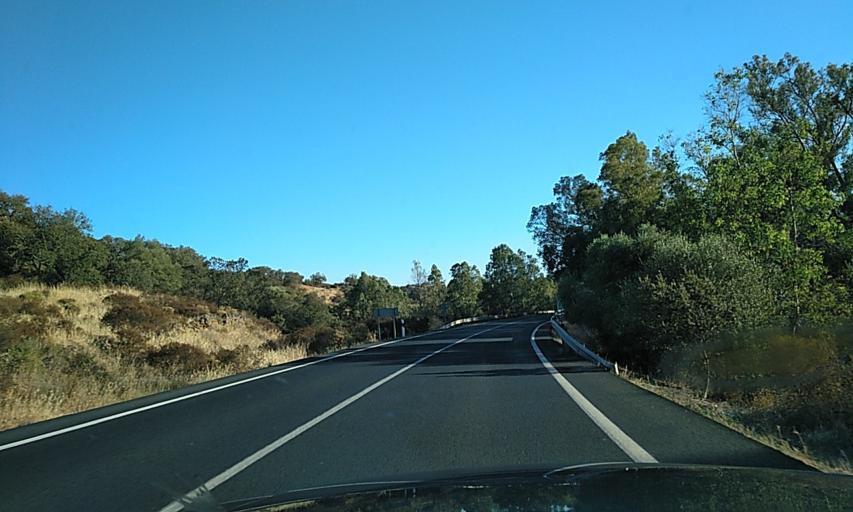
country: ES
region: Andalusia
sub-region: Provincia de Huelva
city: Alosno
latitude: 37.5295
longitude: -7.1330
